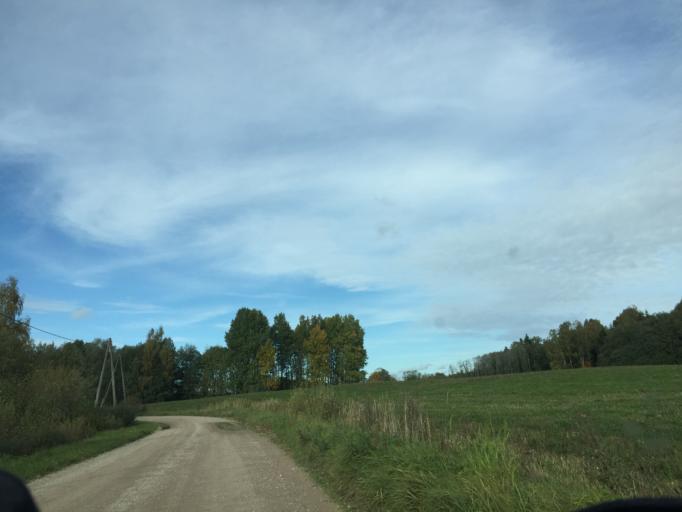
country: LV
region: Jaunpils
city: Jaunpils
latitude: 56.6126
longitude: 23.0449
